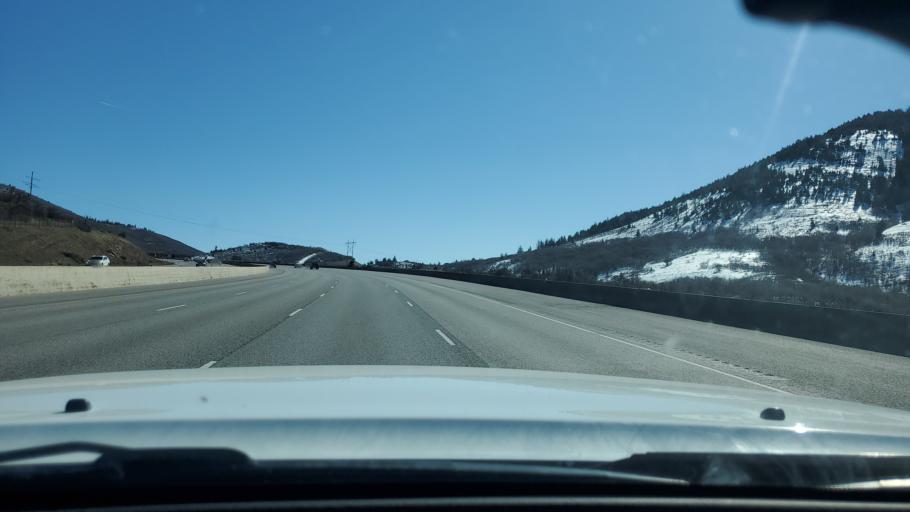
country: US
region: Utah
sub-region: Summit County
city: Summit Park
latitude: 40.7464
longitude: -111.6387
